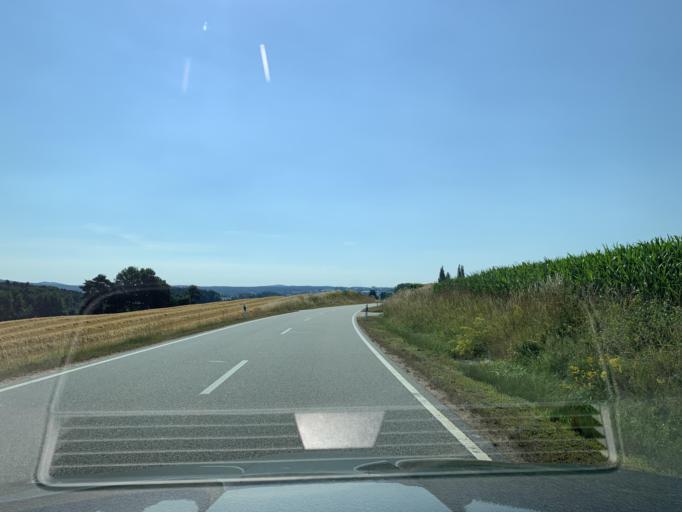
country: DE
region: Bavaria
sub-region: Upper Palatinate
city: Pettendorf
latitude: 49.3596
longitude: 12.3528
